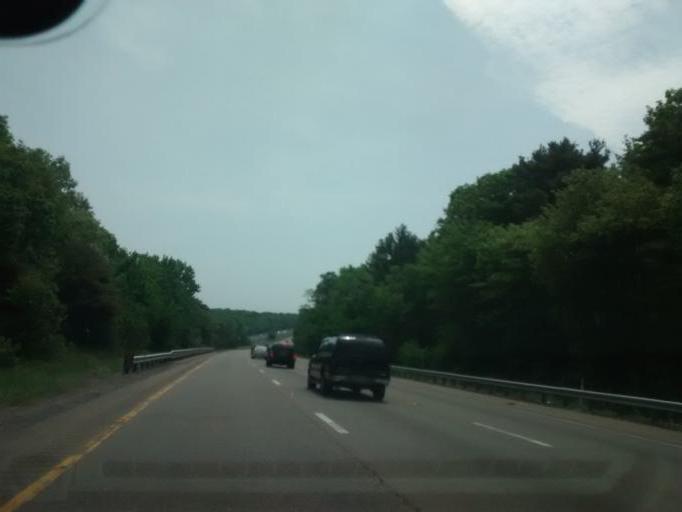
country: US
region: Massachusetts
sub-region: Norfolk County
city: Franklin
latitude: 42.0536
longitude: -71.3730
